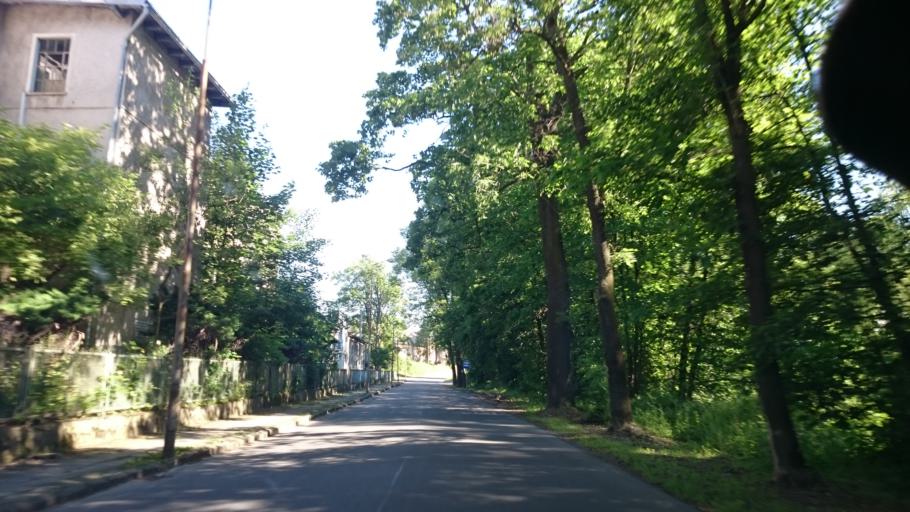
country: PL
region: Lower Silesian Voivodeship
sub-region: Powiat klodzki
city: Bystrzyca Klodzka
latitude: 50.2878
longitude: 16.6444
